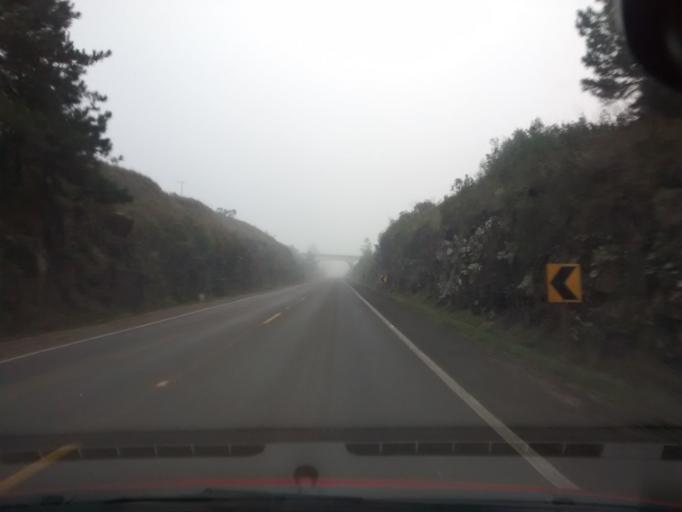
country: BR
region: Rio Grande do Sul
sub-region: Vacaria
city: Vacaria
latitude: -28.4147
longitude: -50.8613
